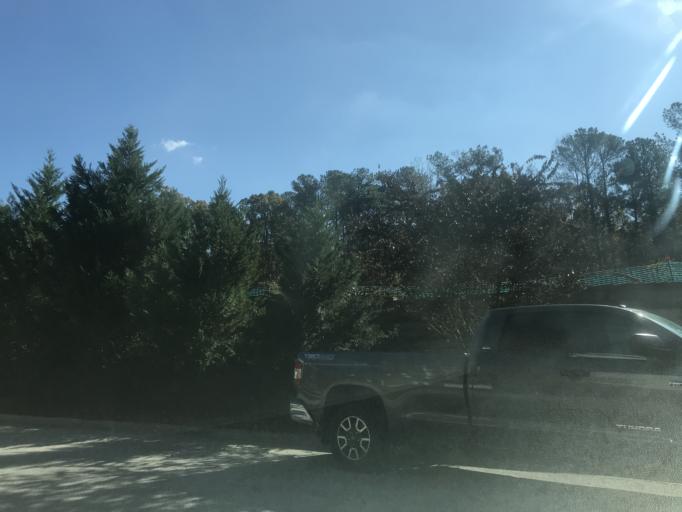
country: US
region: North Carolina
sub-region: Wake County
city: West Raleigh
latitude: 35.8749
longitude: -78.6267
